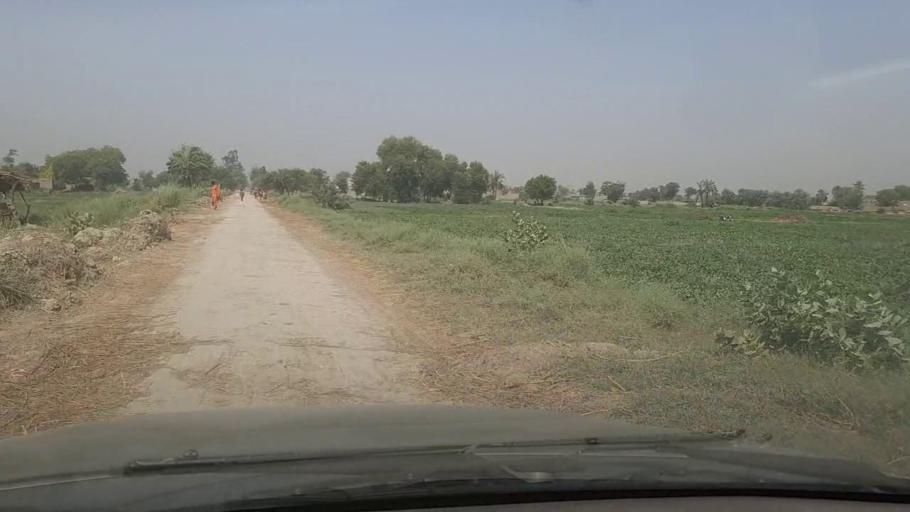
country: PK
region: Sindh
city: Madeji
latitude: 27.7951
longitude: 68.4850
